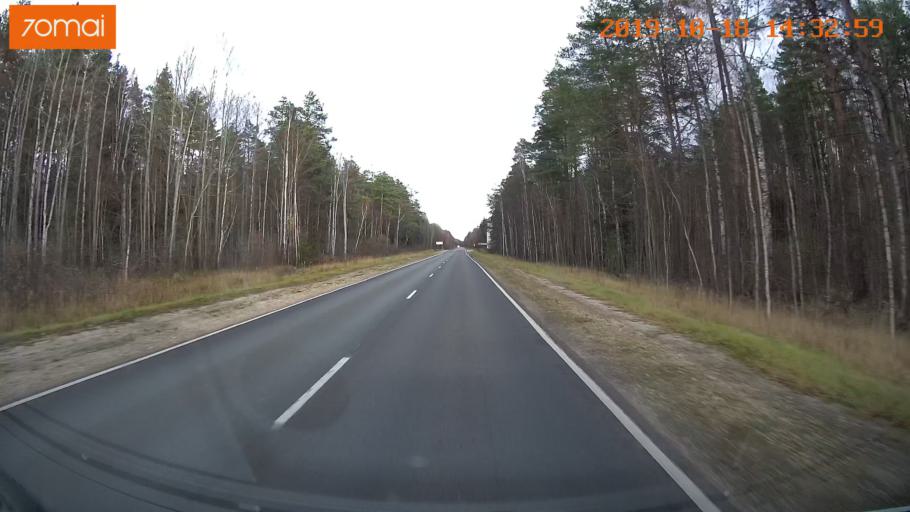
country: RU
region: Rjazan
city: Tuma
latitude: 55.1965
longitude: 40.5886
